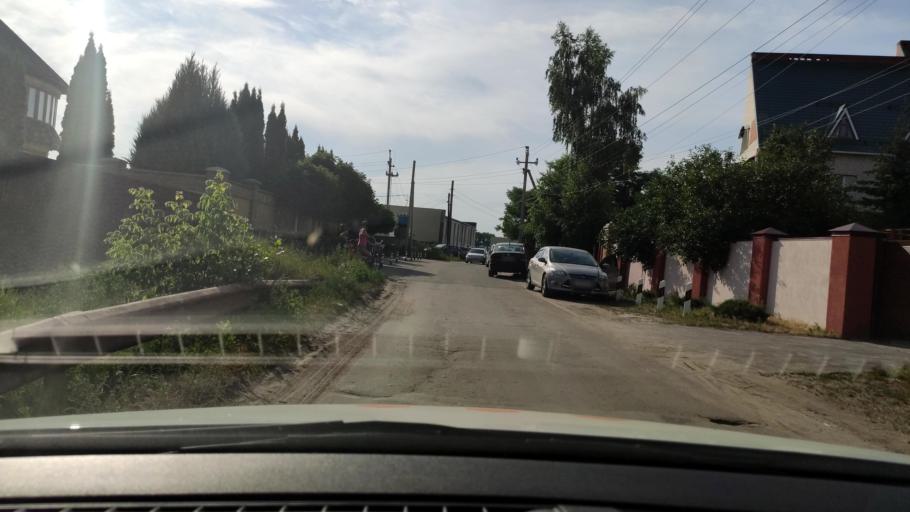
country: RU
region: Voronezj
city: Novaya Usman'
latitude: 51.6294
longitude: 39.4182
